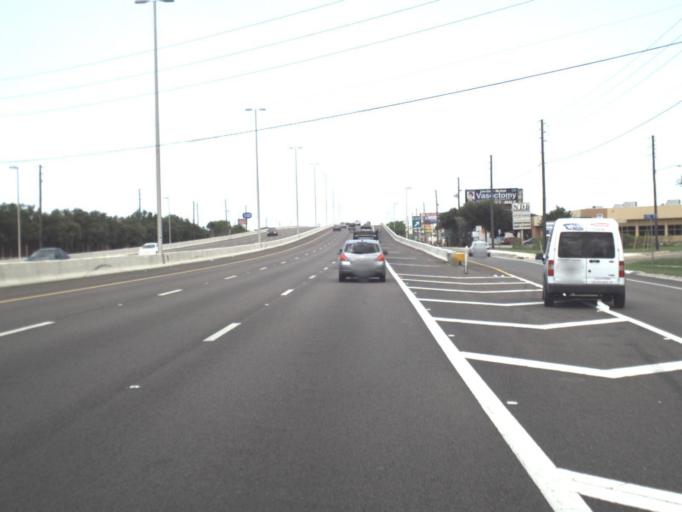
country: US
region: Florida
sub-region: Pinellas County
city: Pinellas Park
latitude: 27.8680
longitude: -82.7041
